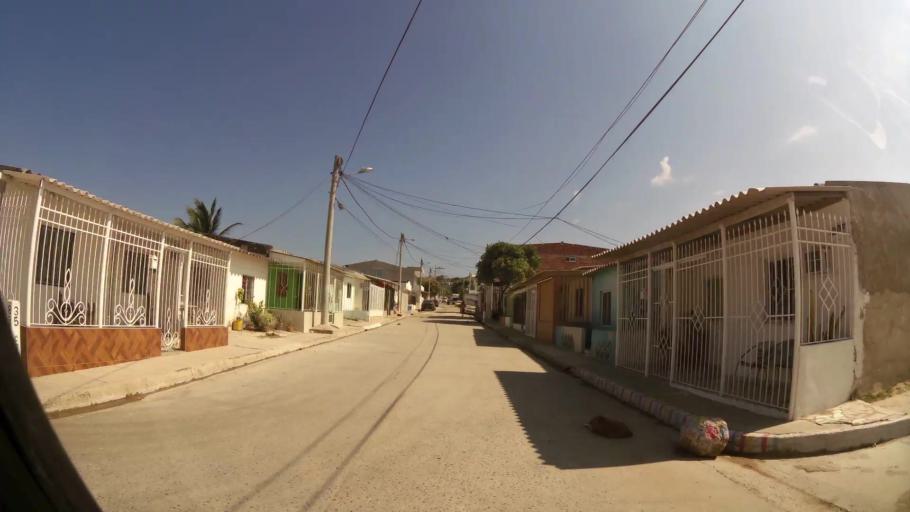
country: CO
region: Atlantico
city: Barranquilla
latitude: 10.9796
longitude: -74.8286
